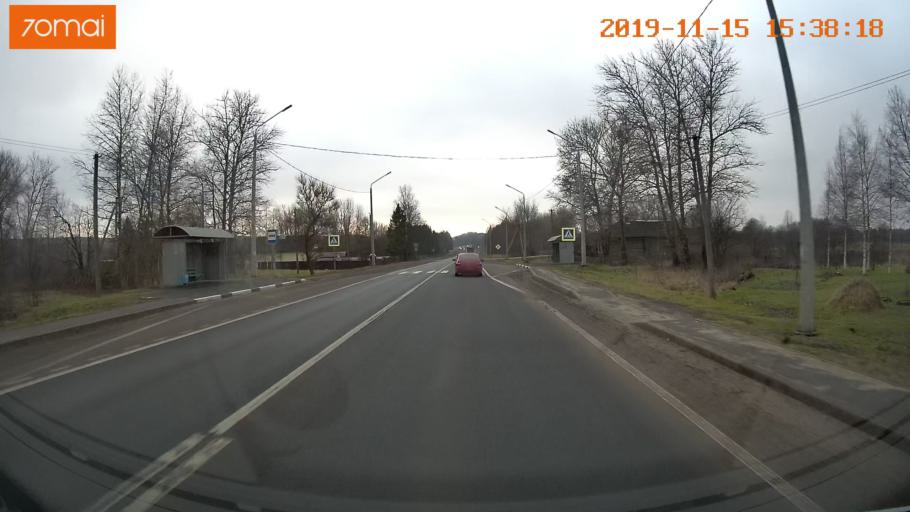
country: RU
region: Jaroslavl
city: Danilov
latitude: 58.0310
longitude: 40.0818
